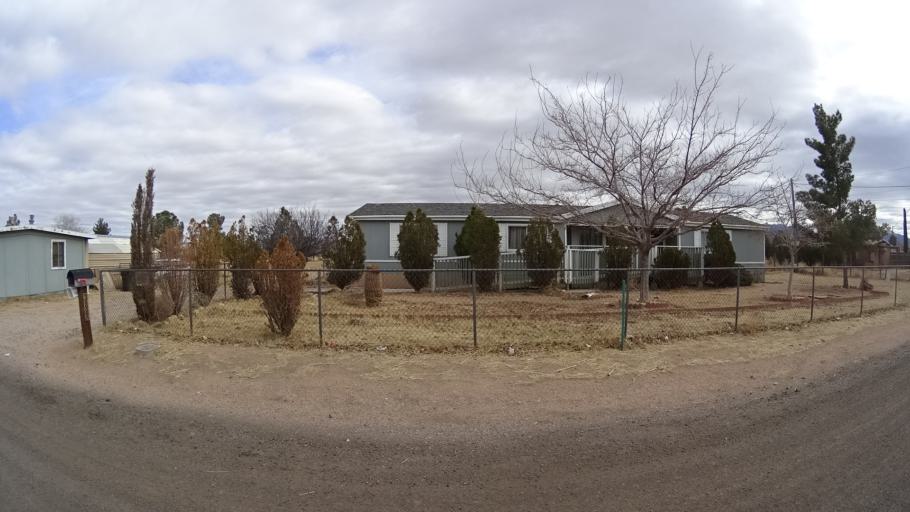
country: US
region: Arizona
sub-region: Mohave County
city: New Kingman-Butler
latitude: 35.2360
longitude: -114.0200
